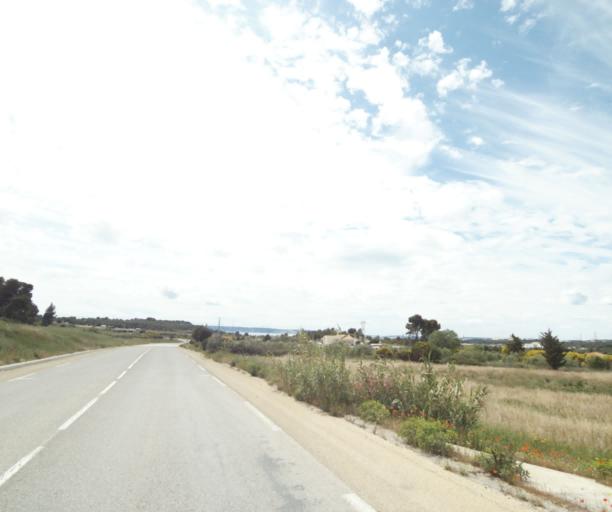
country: FR
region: Provence-Alpes-Cote d'Azur
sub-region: Departement des Bouches-du-Rhone
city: Rognac
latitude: 43.5096
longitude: 5.2403
